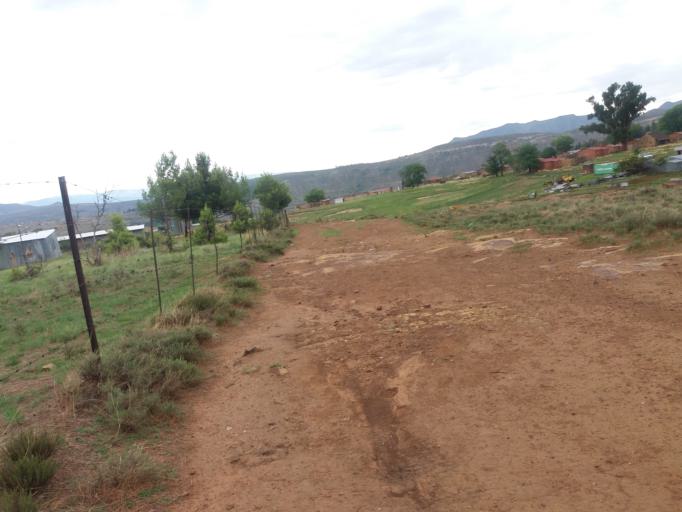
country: LS
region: Quthing
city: Quthing
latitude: -30.4090
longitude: 27.6972
